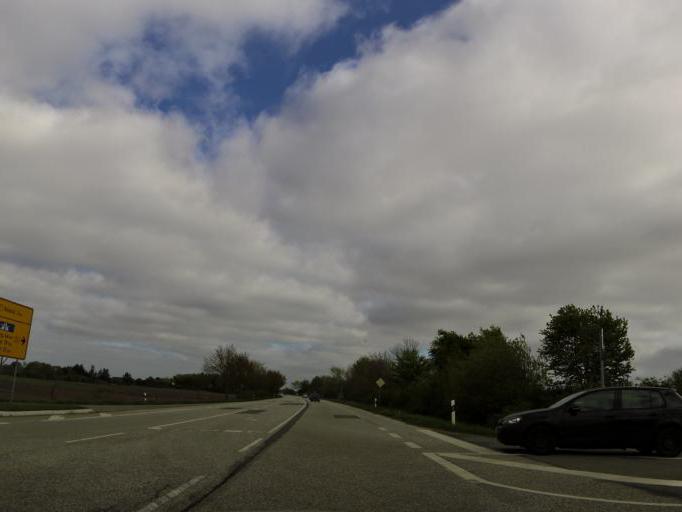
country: DE
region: Schleswig-Holstein
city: Risum-Lindholm
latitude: 54.7717
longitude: 8.8593
